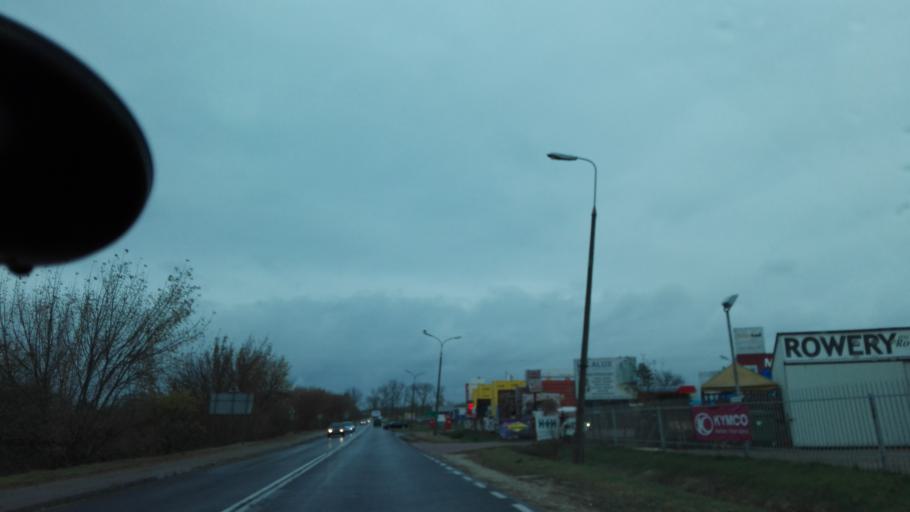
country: PL
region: Lublin Voivodeship
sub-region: Powiat pulawski
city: Pulawy
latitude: 51.4111
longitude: 21.9360
